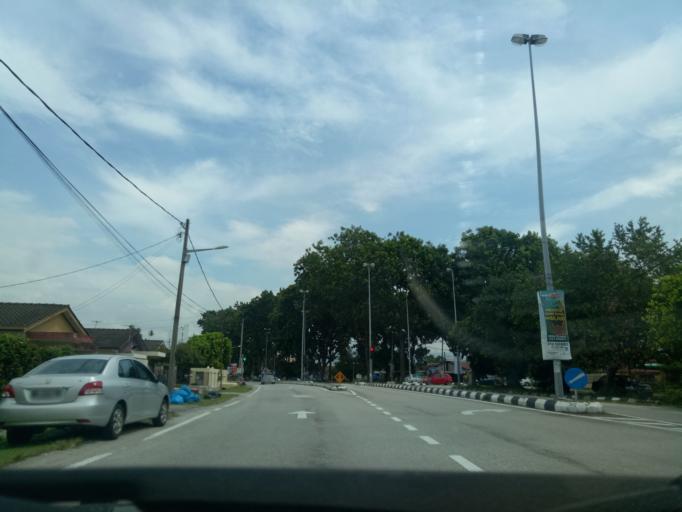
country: MY
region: Perak
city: Ipoh
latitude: 4.6112
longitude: 101.1151
